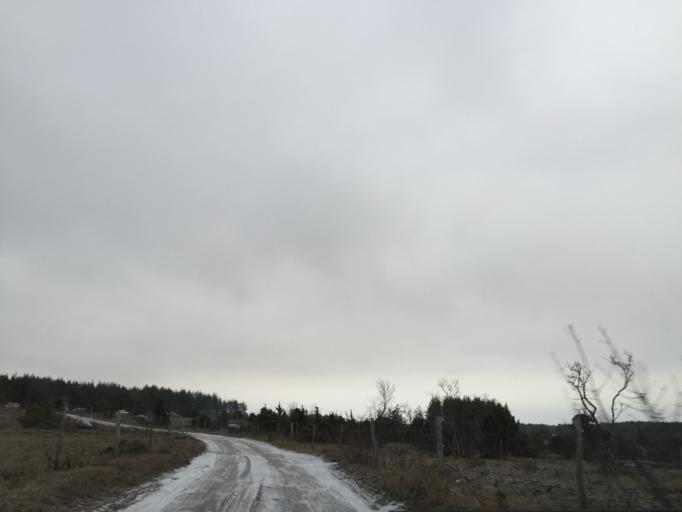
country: EE
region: Saare
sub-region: Orissaare vald
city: Orissaare
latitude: 58.6102
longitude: 23.0890
